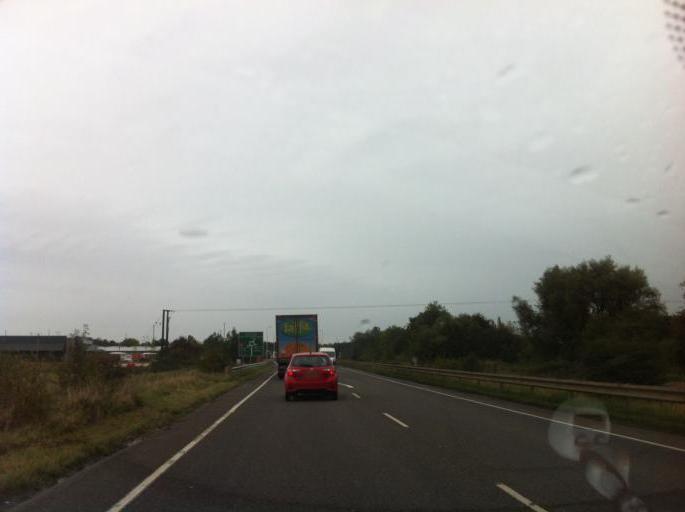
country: GB
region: England
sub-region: Lincolnshire
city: Kirton
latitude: 52.8872
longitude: -0.0860
